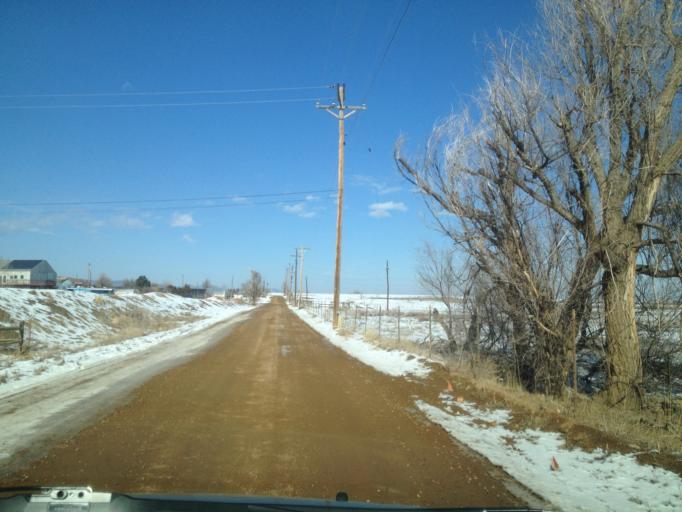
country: US
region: Colorado
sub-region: Boulder County
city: Boulder
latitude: 40.0592
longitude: -105.2634
